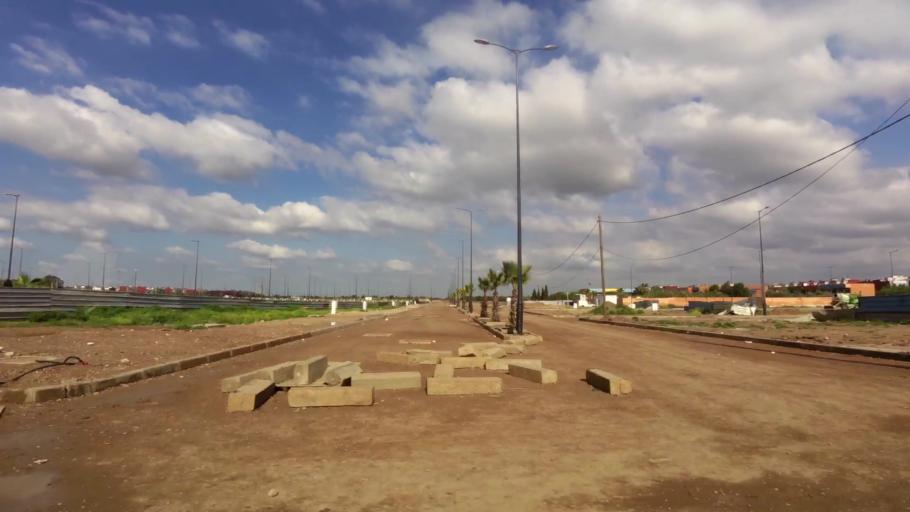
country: MA
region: Chaouia-Ouardigha
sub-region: Settat Province
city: Berrechid
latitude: 33.2660
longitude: -7.5715
